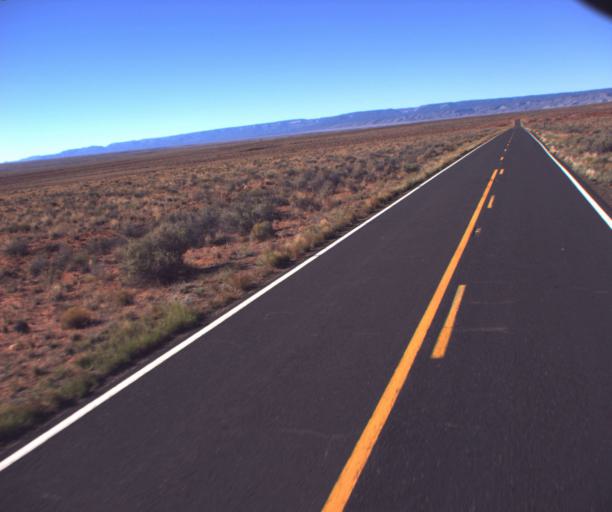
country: US
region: Arizona
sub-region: Coconino County
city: LeChee
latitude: 36.6948
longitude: -111.8113
